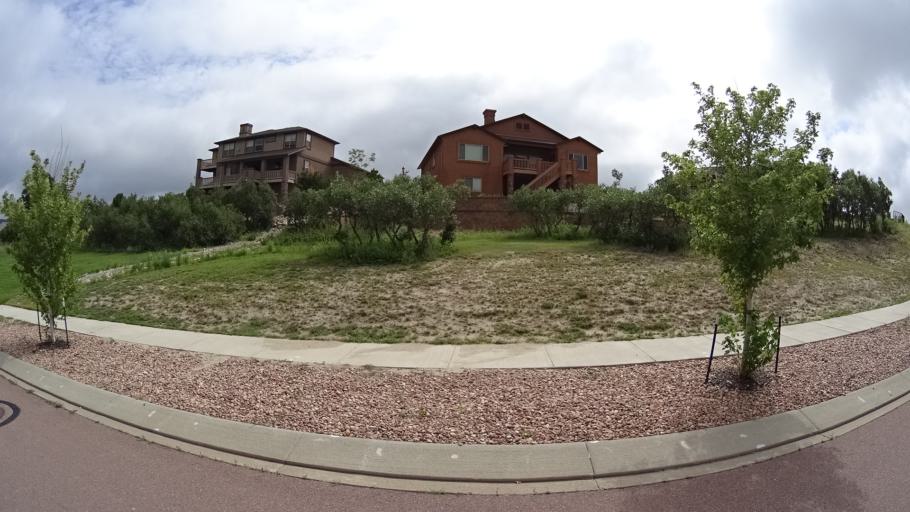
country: US
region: Colorado
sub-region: El Paso County
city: Gleneagle
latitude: 39.0146
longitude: -104.7889
